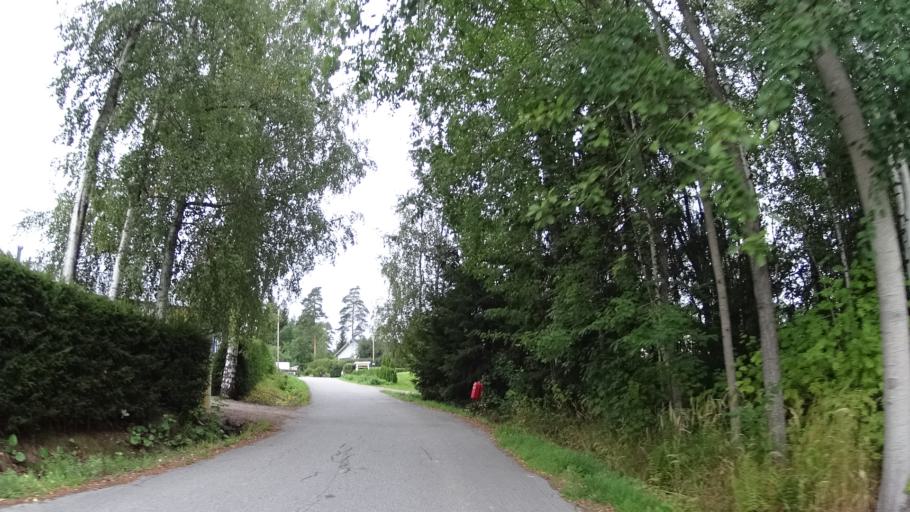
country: FI
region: Uusimaa
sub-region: Helsinki
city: Kilo
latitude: 60.3221
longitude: 24.8472
